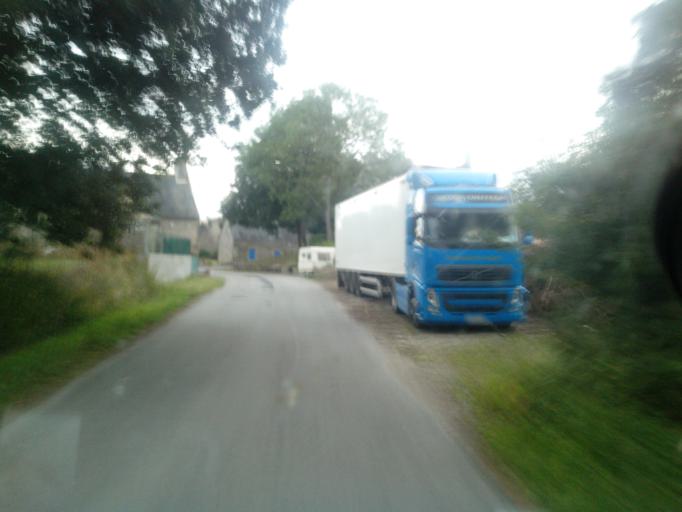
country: FR
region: Brittany
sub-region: Departement du Morbihan
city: Plumelec
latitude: 47.8931
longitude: -2.6374
